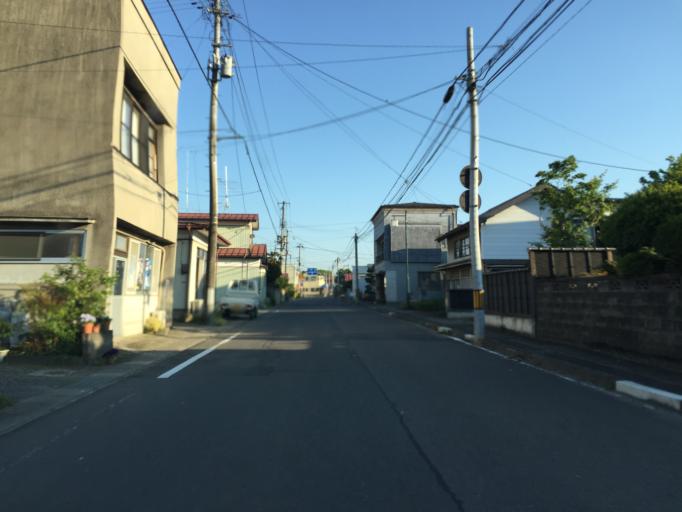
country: JP
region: Fukushima
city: Ishikawa
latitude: 37.0831
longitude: 140.4164
